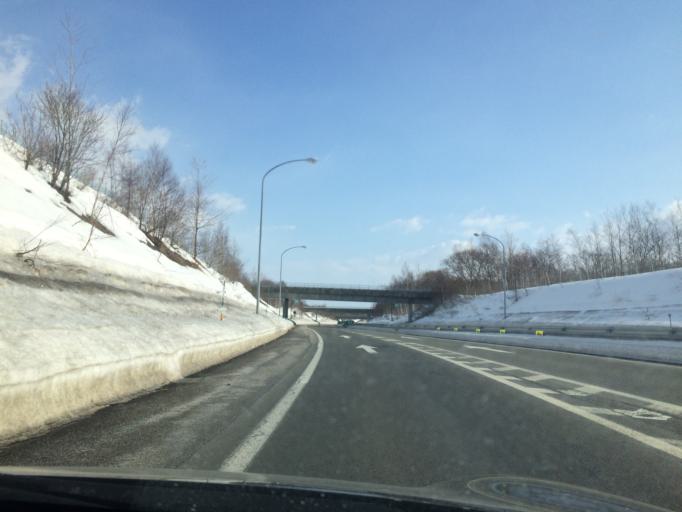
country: JP
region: Hokkaido
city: Chitose
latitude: 42.8471
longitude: 141.5881
